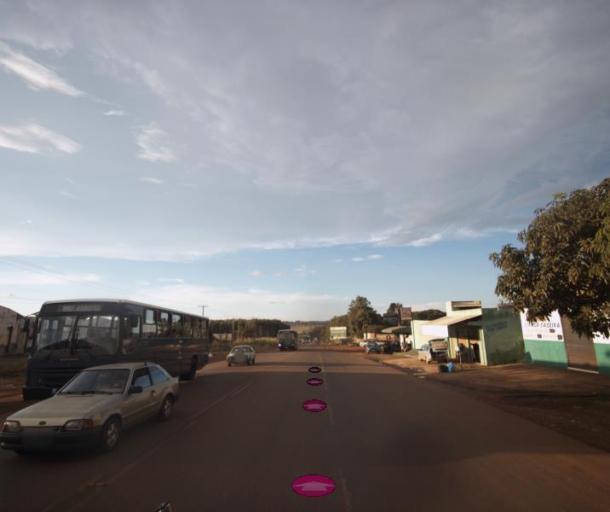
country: BR
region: Goias
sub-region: Anapolis
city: Anapolis
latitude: -16.2843
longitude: -48.9432
